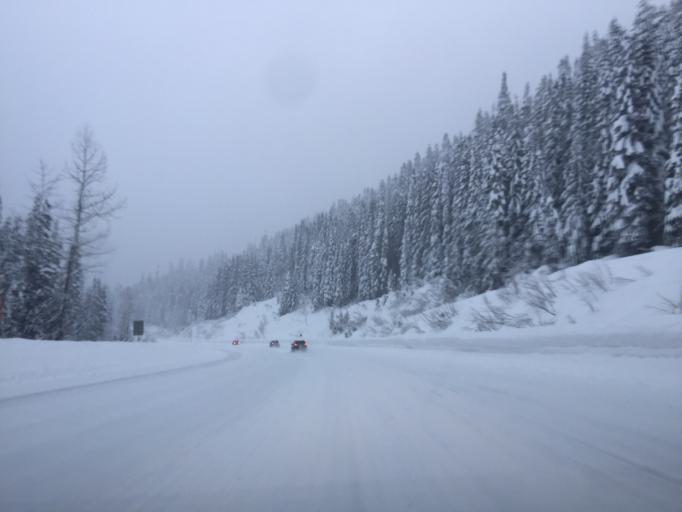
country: US
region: Washington
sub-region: Chelan County
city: Leavenworth
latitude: 47.7810
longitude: -121.0498
